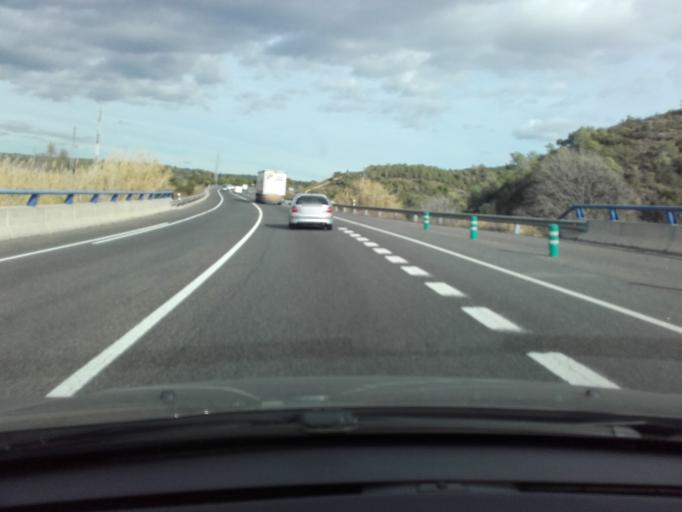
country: ES
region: Catalonia
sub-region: Provincia de Tarragona
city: Altafulla
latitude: 41.1512
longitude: 1.3659
